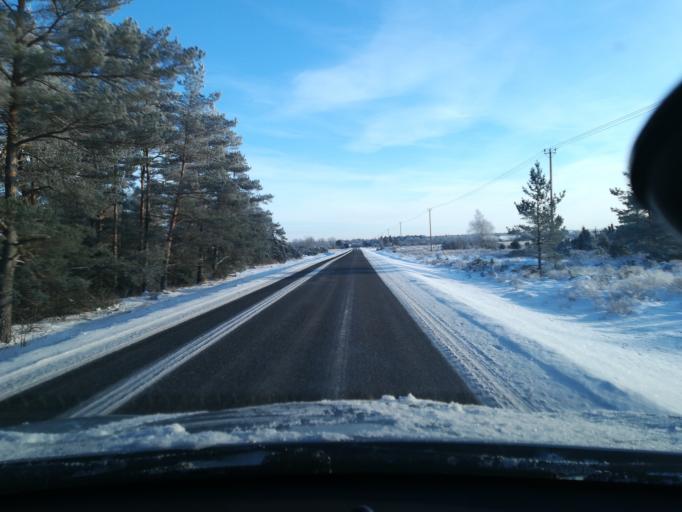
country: EE
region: Harju
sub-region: Keila linn
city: Keila
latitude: 59.3916
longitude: 24.3928
